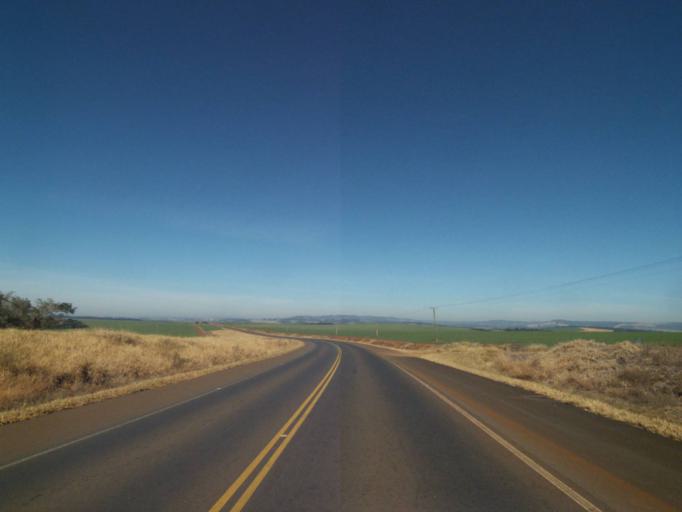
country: BR
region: Parana
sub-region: Tibagi
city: Tibagi
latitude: -24.4388
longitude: -50.4225
